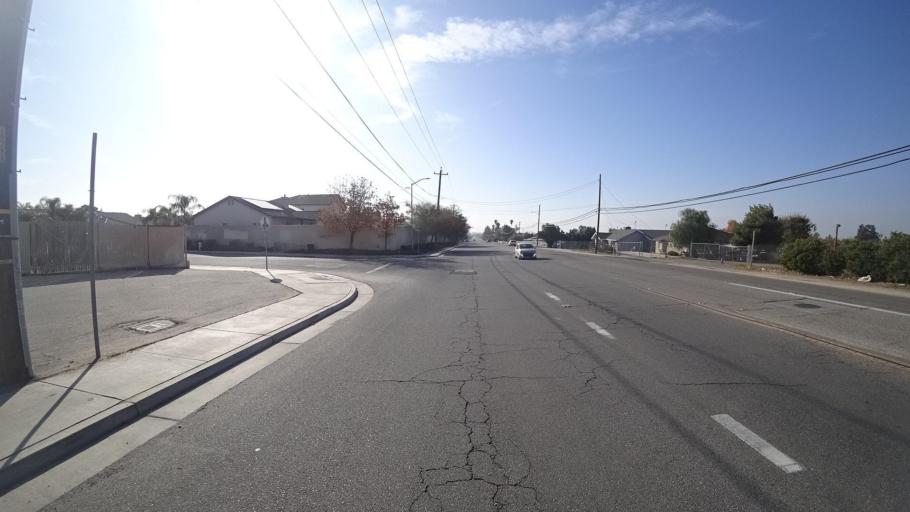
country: US
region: California
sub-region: Kern County
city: Bakersfield
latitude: 35.3743
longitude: -118.9141
